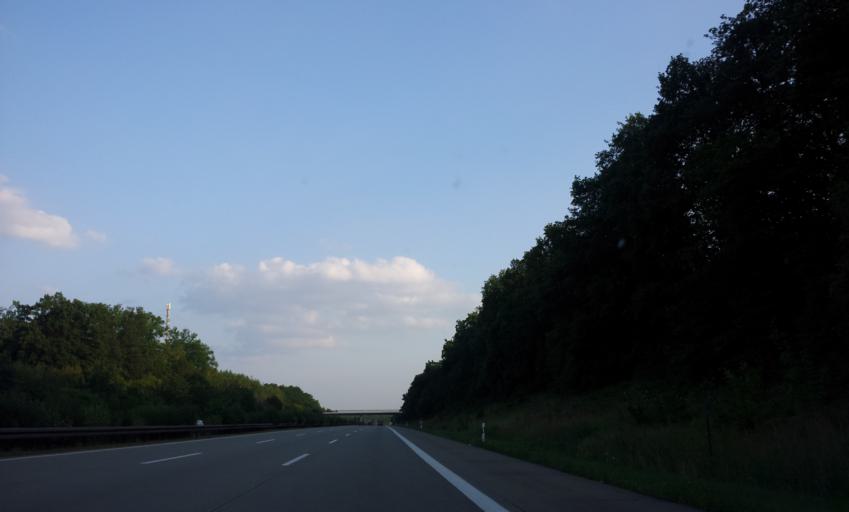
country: DE
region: Brandenburg
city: Woltersdorf
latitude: 52.4547
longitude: 13.7987
